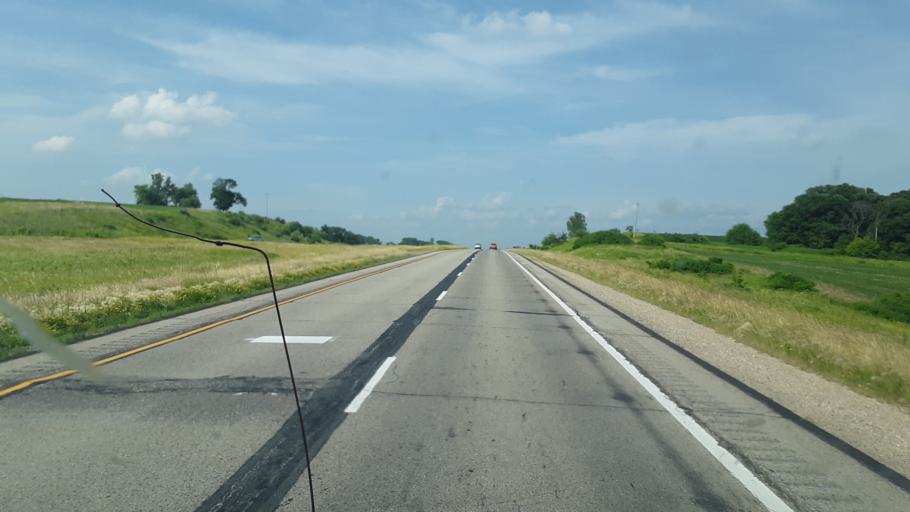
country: US
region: Iowa
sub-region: Jasper County
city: Baxter
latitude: 41.8881
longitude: -93.1961
